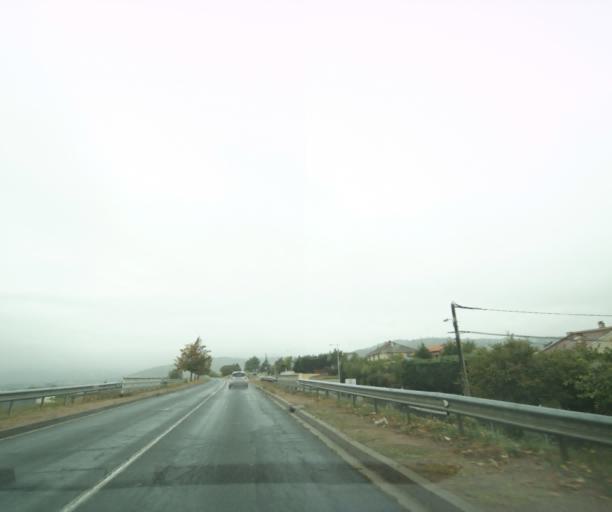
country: FR
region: Auvergne
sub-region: Departement du Puy-de-Dome
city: Cebazat
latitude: 45.8354
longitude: 3.1021
